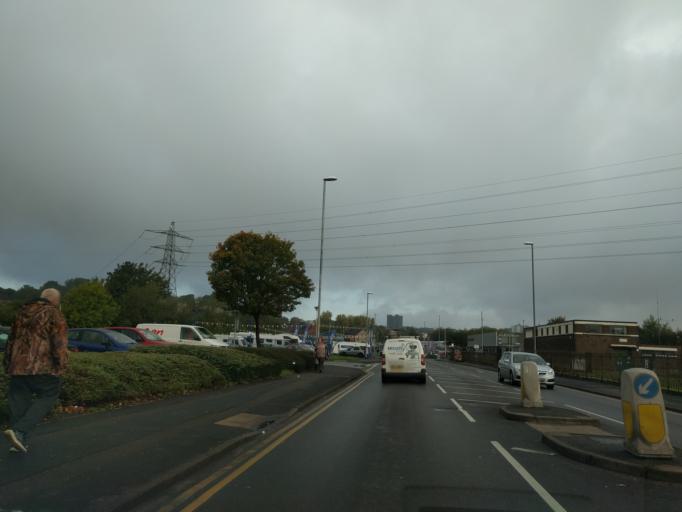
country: GB
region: England
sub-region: Stoke-on-Trent
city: Stoke-on-Trent
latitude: 53.0120
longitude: -2.1671
